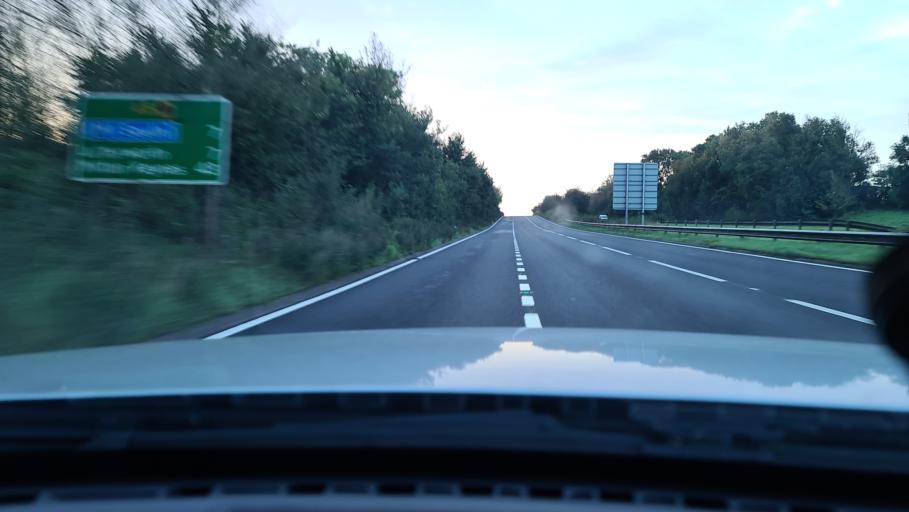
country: GB
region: England
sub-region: Leicestershire
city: Sapcote
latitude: 52.5009
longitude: -1.3227
